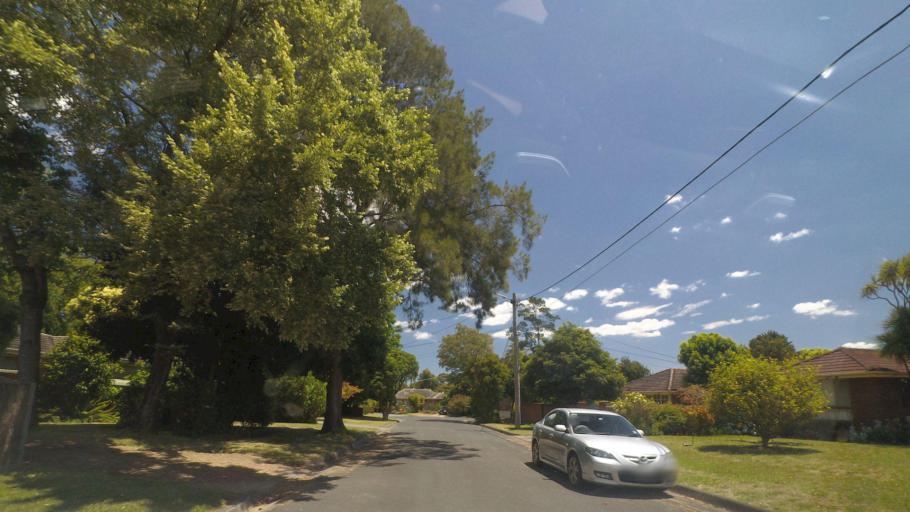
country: AU
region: Victoria
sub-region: Maroondah
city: Kilsyth South
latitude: -37.8114
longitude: 145.3208
